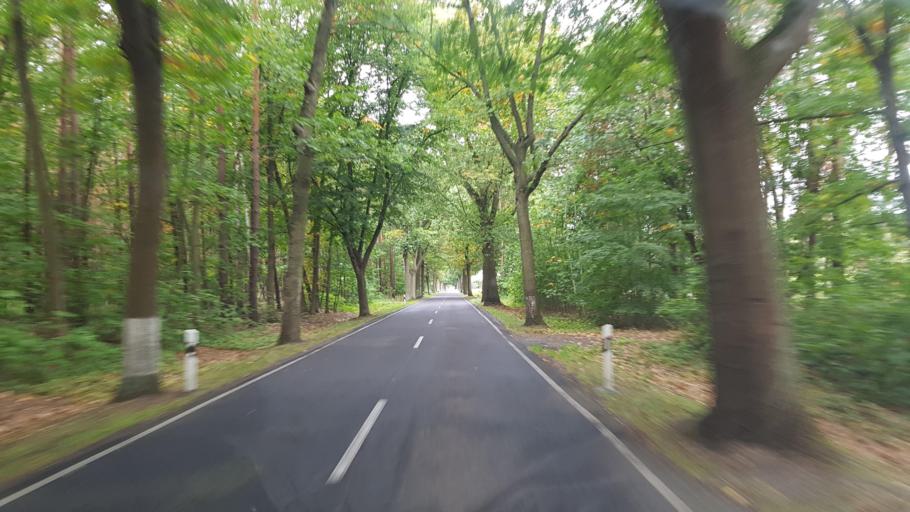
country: DE
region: Brandenburg
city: Kasel-Golzig
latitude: 51.9349
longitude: 13.6810
